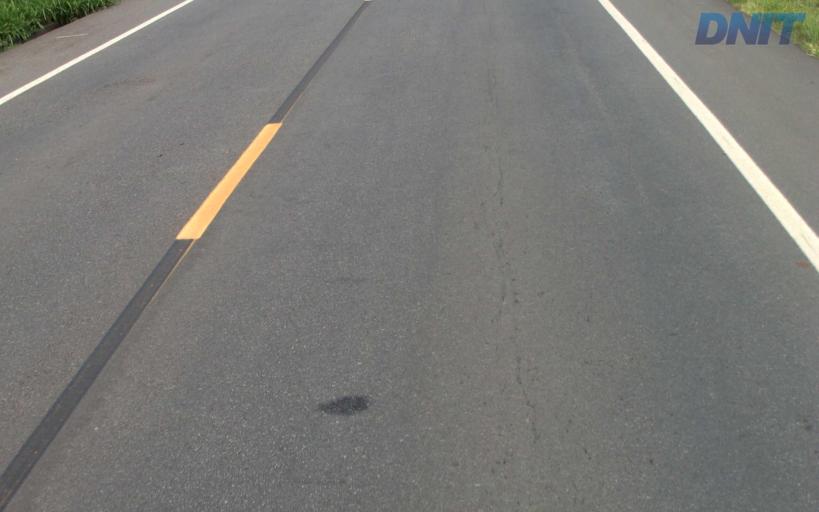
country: BR
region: Minas Gerais
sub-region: Belo Oriente
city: Belo Oriente
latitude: -19.2044
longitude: -42.2944
